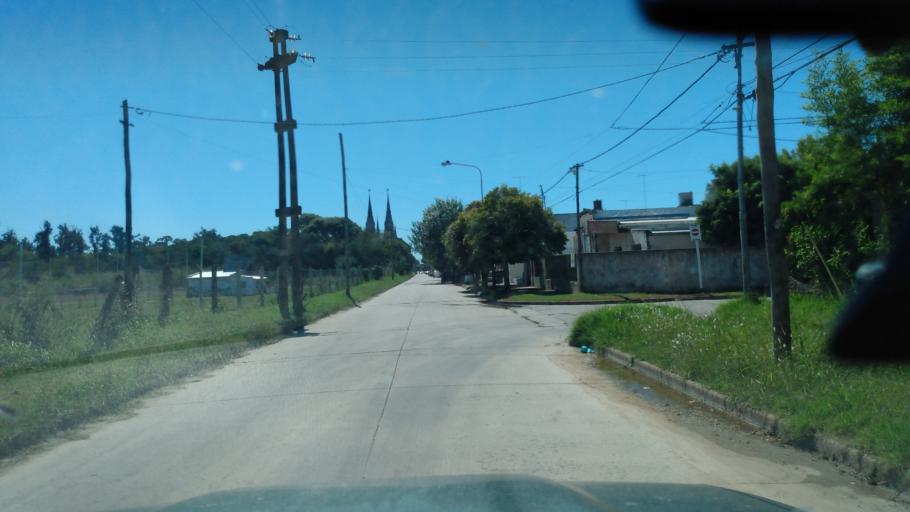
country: AR
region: Buenos Aires
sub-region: Partido de Lujan
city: Lujan
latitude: -34.5719
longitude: -59.1240
